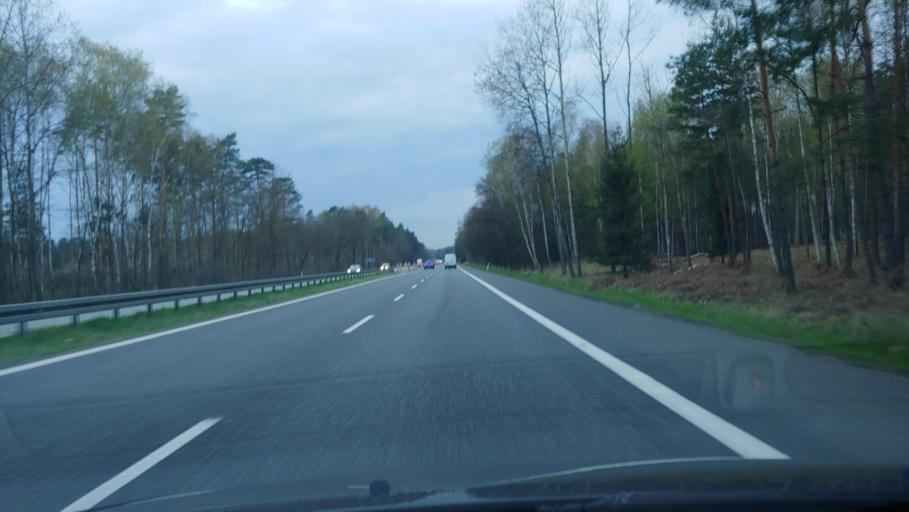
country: PL
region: Silesian Voivodeship
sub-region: Powiat bierunsko-ledzinski
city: Bierun
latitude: 50.1410
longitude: 19.0748
